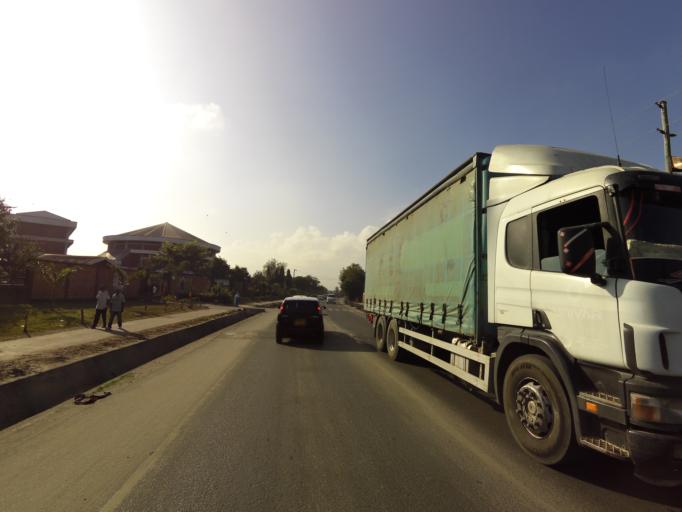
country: TZ
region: Dar es Salaam
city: Magomeni
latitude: -6.8142
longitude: 39.2300
